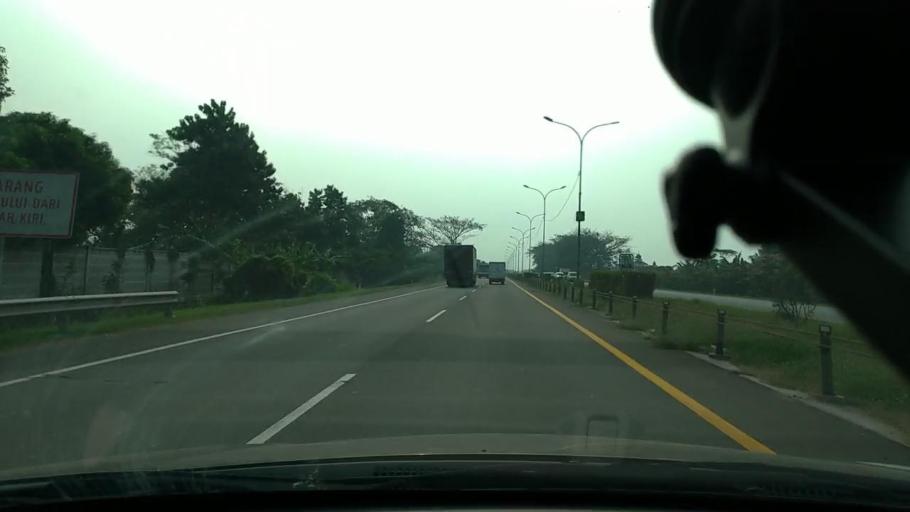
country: ID
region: Banten
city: Serang
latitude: -6.1068
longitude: 106.1778
